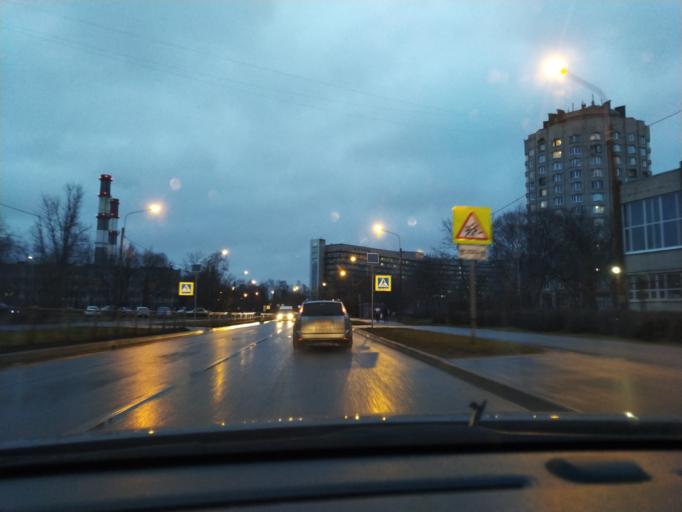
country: RU
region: St.-Petersburg
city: Uritsk
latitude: 59.8344
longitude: 30.1825
